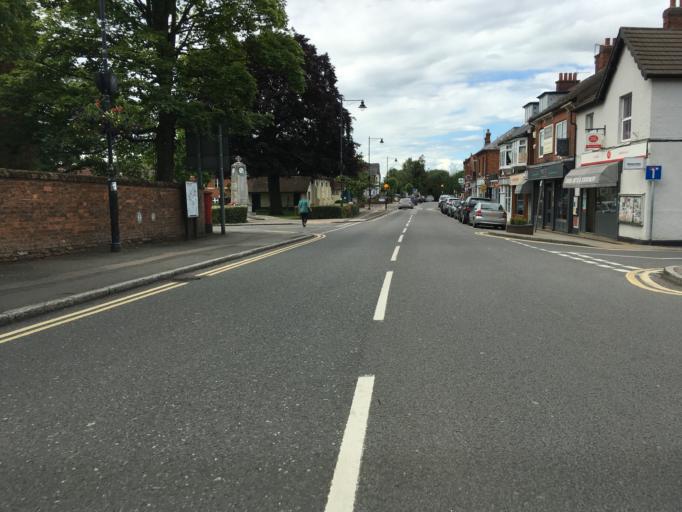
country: GB
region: England
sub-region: Milton Keynes
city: Woburn Sands
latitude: 52.0113
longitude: -0.6469
